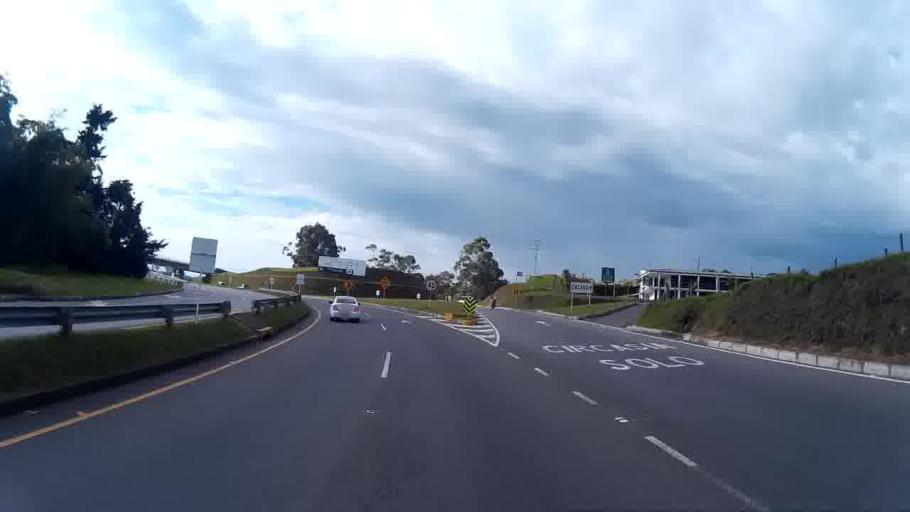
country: CO
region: Quindio
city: Circasia
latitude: 4.6042
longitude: -75.6349
